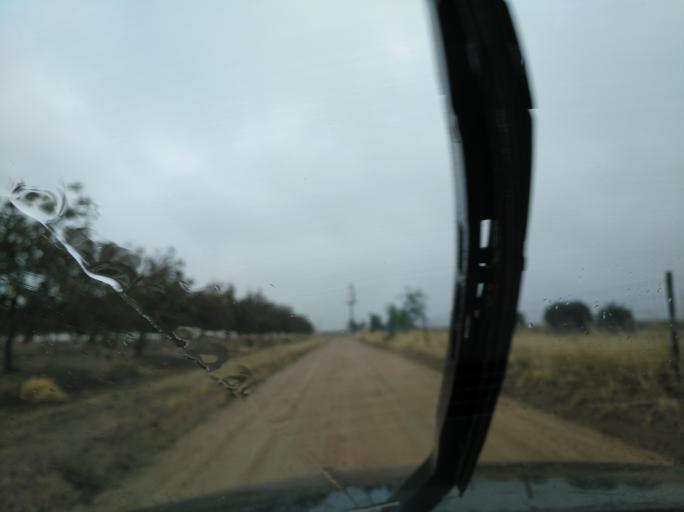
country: PT
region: Portalegre
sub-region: Campo Maior
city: Campo Maior
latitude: 38.9573
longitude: -7.0443
